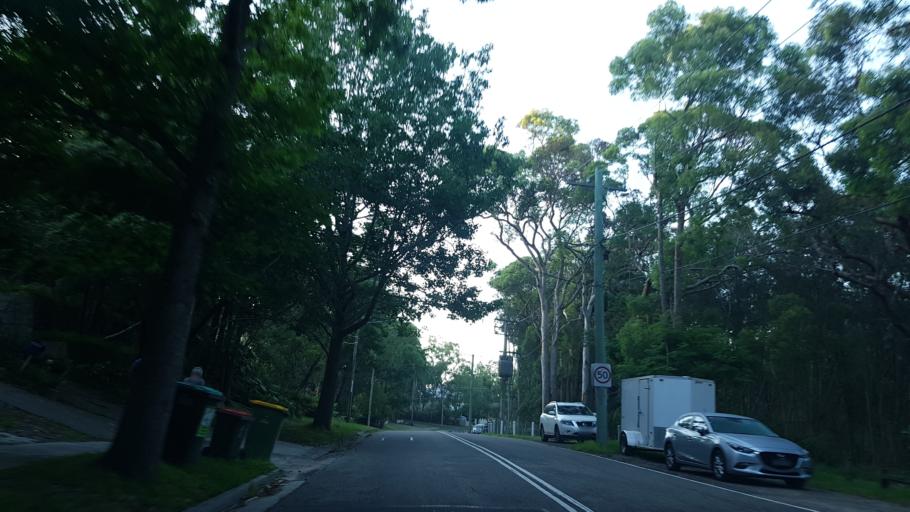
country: AU
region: New South Wales
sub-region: Warringah
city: Narrabeen
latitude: -33.7274
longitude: 151.2766
